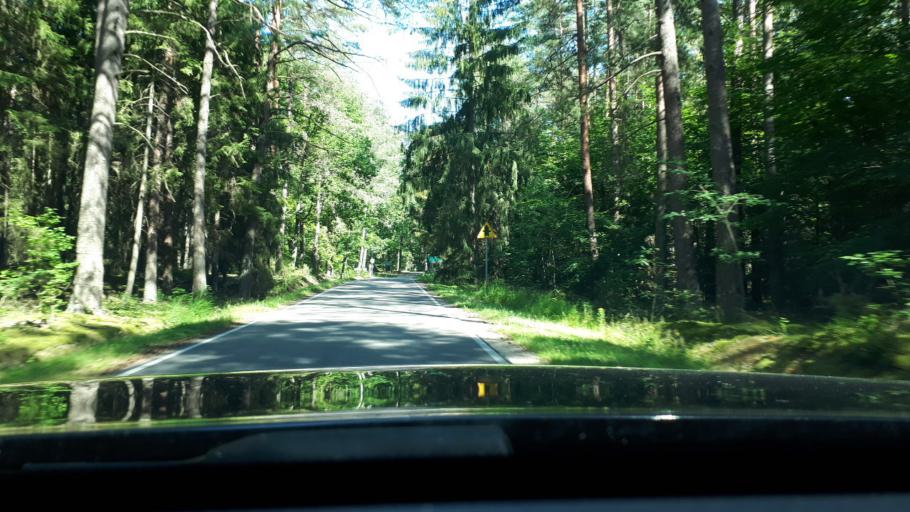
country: PL
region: Warmian-Masurian Voivodeship
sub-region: Powiat olsztynski
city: Stawiguda
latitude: 53.5886
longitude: 20.4476
